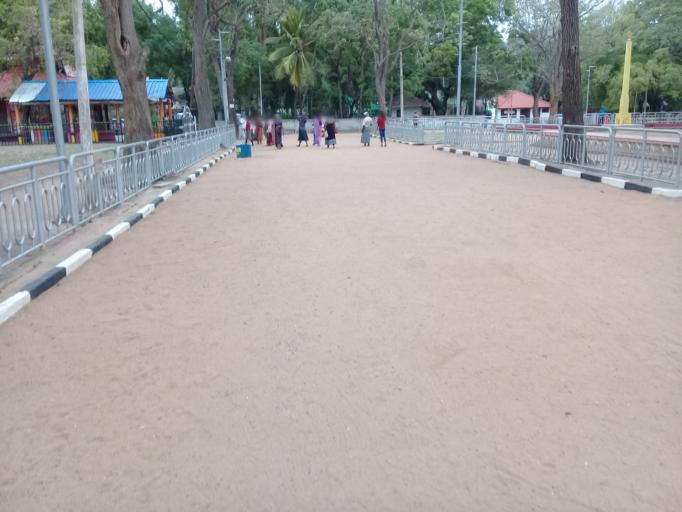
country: LK
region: Uva
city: Wattegama
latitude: 6.4171
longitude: 81.3349
